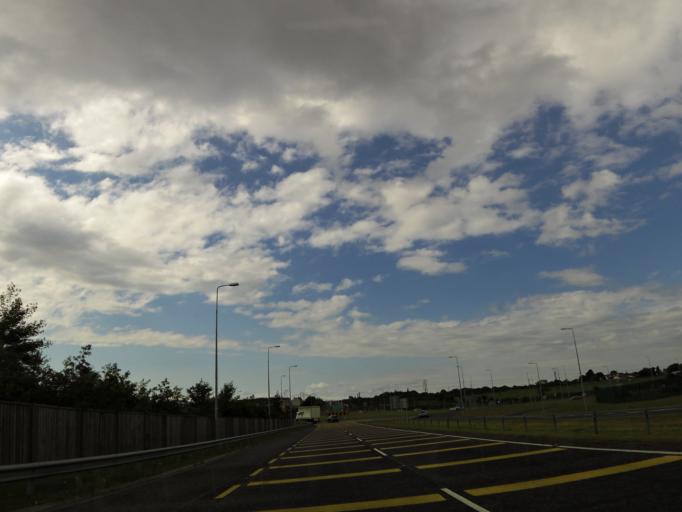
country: IE
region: Connaught
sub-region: County Galway
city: Oranmore
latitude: 53.2841
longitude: -8.9782
